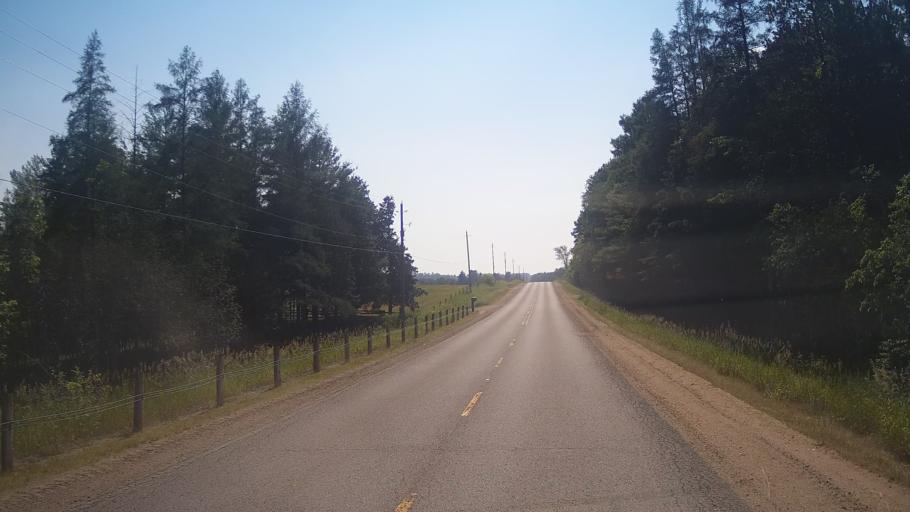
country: CA
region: Ontario
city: Pembroke
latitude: 45.6138
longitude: -77.1906
